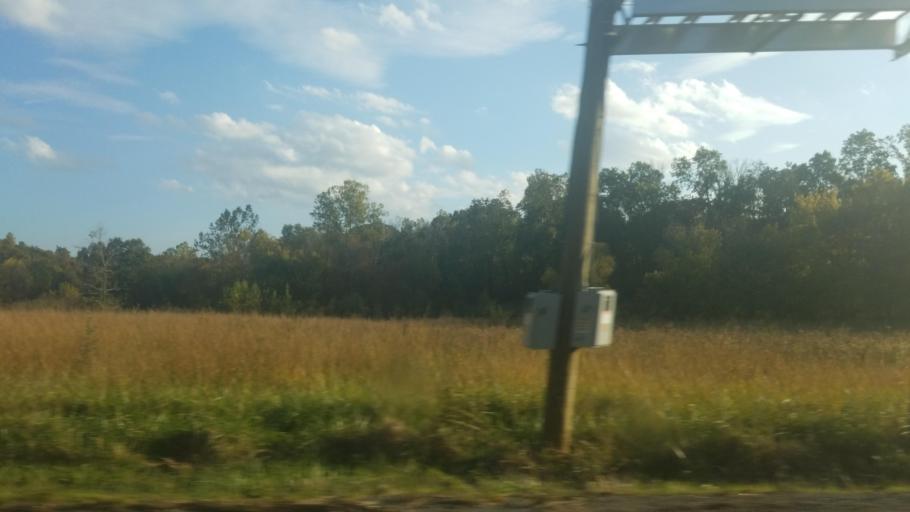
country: US
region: Illinois
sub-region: Saline County
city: Carrier Mills
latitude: 37.7708
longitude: -88.7648
